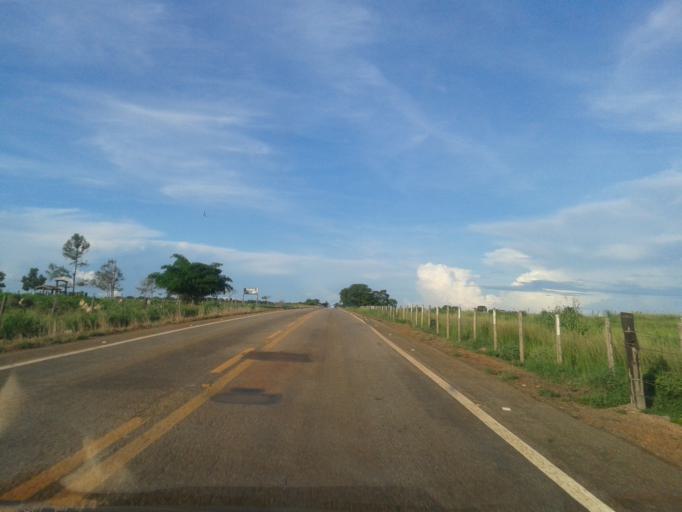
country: BR
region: Goias
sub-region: Sao Miguel Do Araguaia
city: Sao Miguel do Araguaia
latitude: -13.4370
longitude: -50.2858
